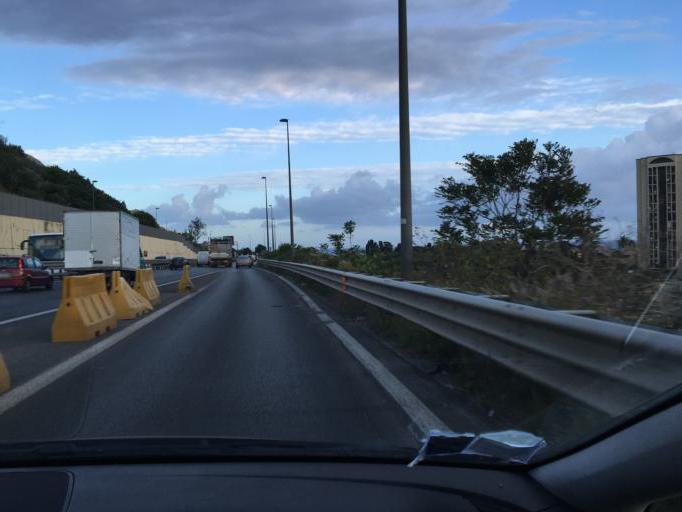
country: IT
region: Sicily
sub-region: Palermo
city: Isola delle Femmine
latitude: 38.1925
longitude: 13.2808
